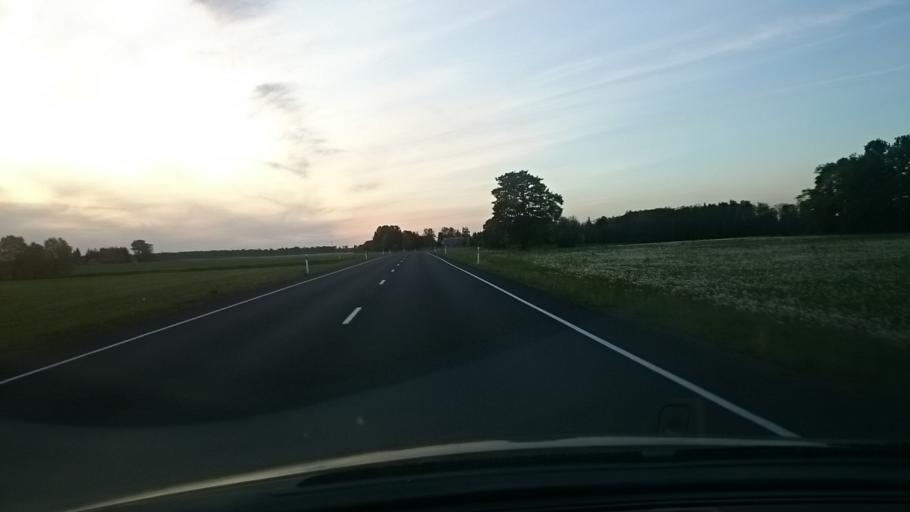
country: EE
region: Viljandimaa
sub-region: Vohma linn
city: Vohma
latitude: 58.6708
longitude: 25.6063
